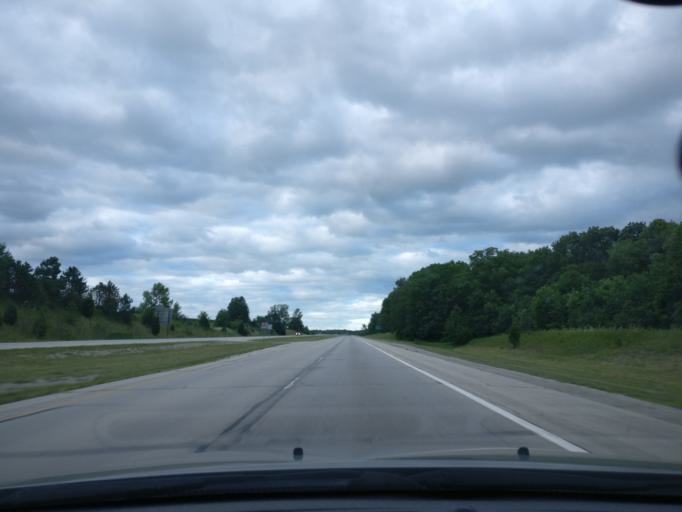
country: US
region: Ohio
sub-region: Greene County
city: Xenia
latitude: 39.6709
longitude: -83.9039
